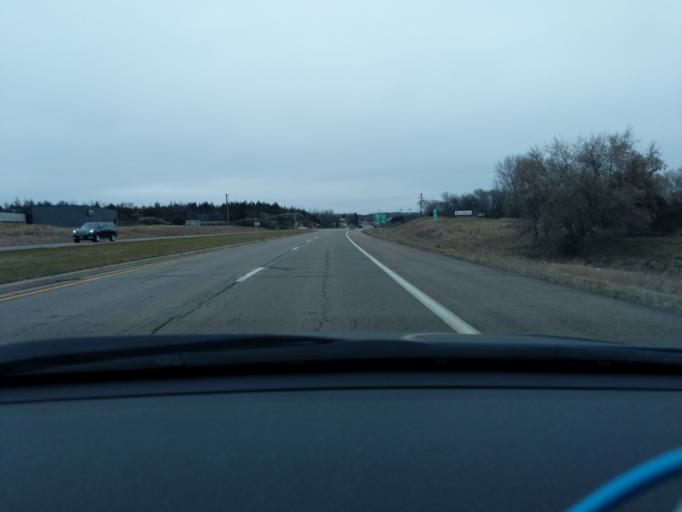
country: US
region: Minnesota
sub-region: Yellow Medicine County
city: Granite Falls
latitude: 44.8002
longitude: -95.5479
